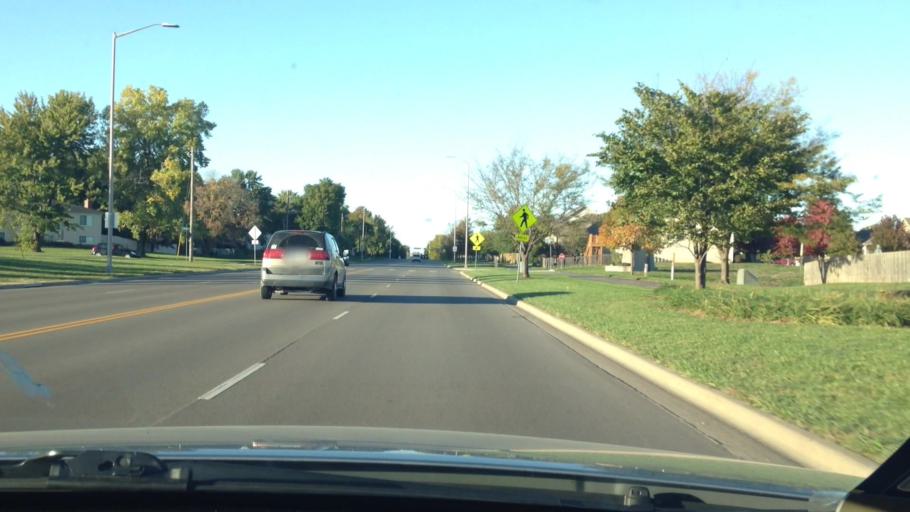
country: US
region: Kansas
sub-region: Johnson County
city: Gardner
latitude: 38.7988
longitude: -94.9275
